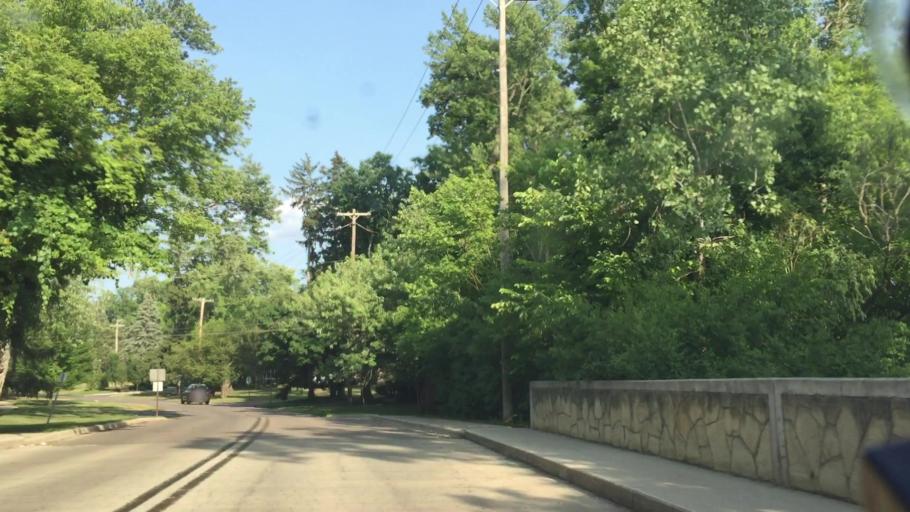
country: US
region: Michigan
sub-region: Oakland County
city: Beverly Hills
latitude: 42.5276
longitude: -83.2420
